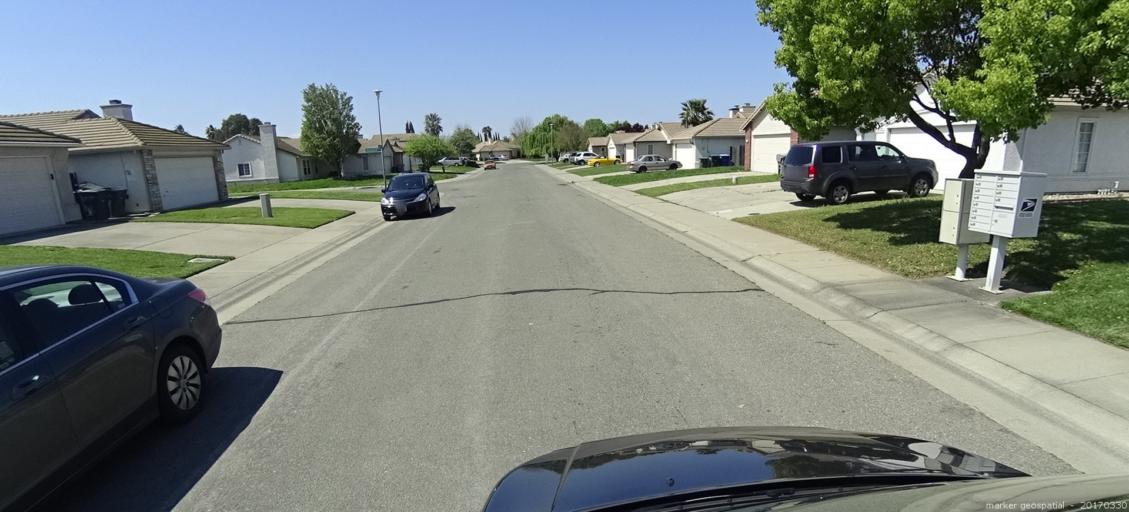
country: US
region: California
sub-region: Sacramento County
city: Florin
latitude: 38.4594
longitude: -121.4195
